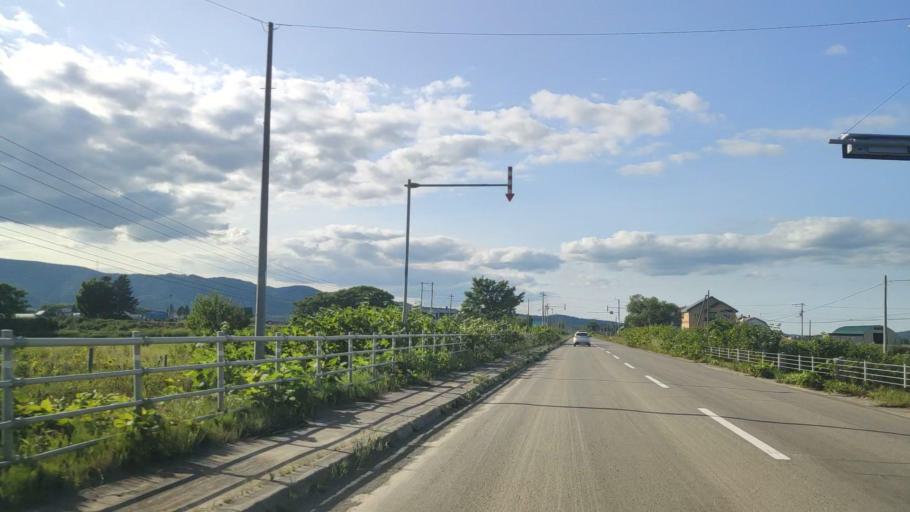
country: JP
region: Hokkaido
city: Makubetsu
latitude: 44.8227
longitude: 142.0658
